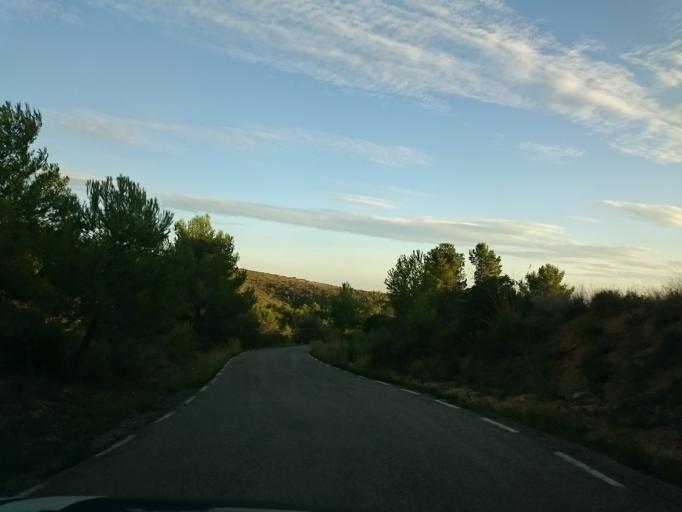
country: ES
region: Catalonia
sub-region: Provincia de Barcelona
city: Olivella
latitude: 41.3071
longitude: 1.8350
